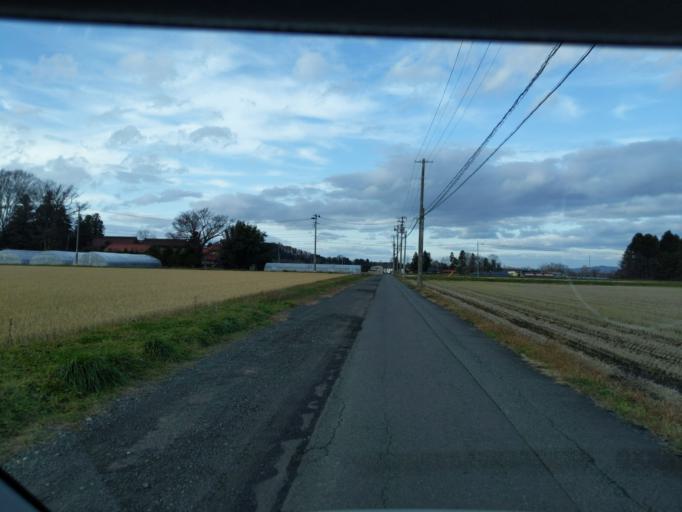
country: JP
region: Iwate
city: Mizusawa
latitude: 39.1590
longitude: 141.0892
